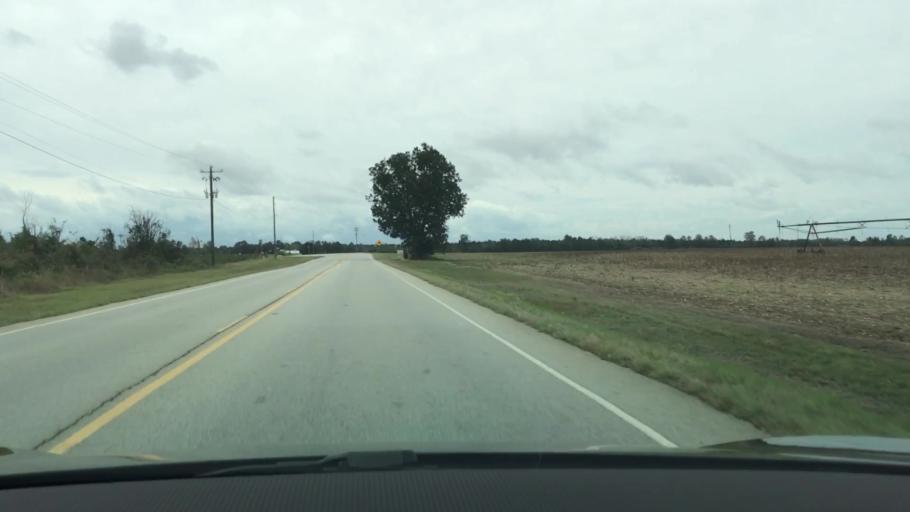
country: US
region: Georgia
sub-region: Jefferson County
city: Louisville
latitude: 33.1038
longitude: -82.4242
